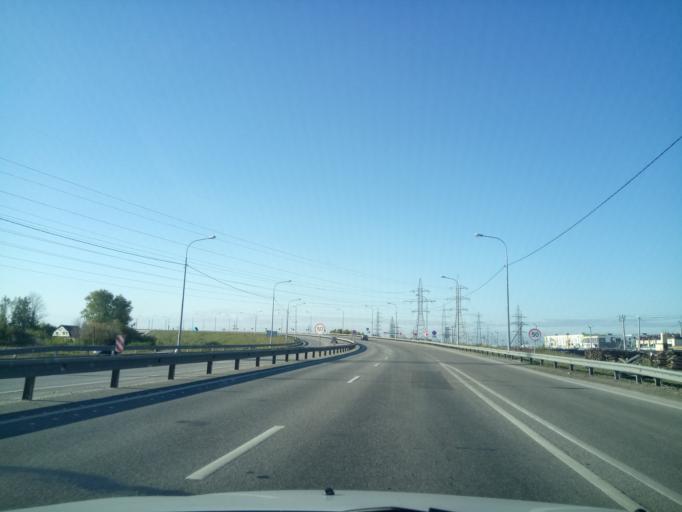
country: RU
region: Nizjnij Novgorod
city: Burevestnik
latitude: 56.1822
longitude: 43.9166
